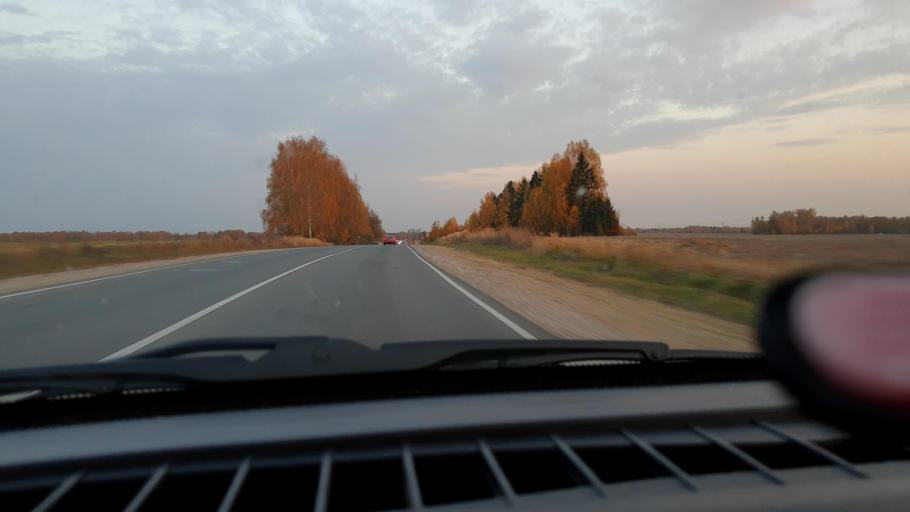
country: RU
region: Nizjnij Novgorod
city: Gorodets
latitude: 56.6276
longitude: 43.5439
